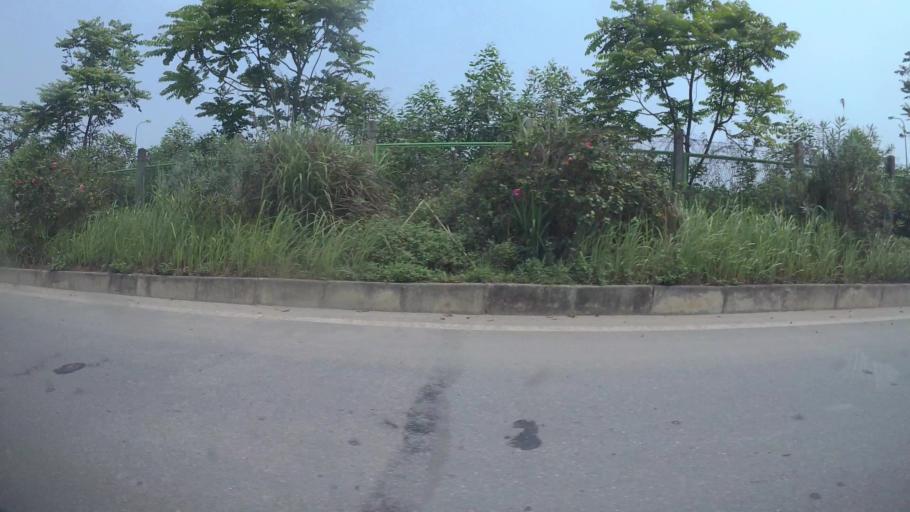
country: VN
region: Ha Noi
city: Quoc Oai
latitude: 21.0005
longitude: 105.6035
